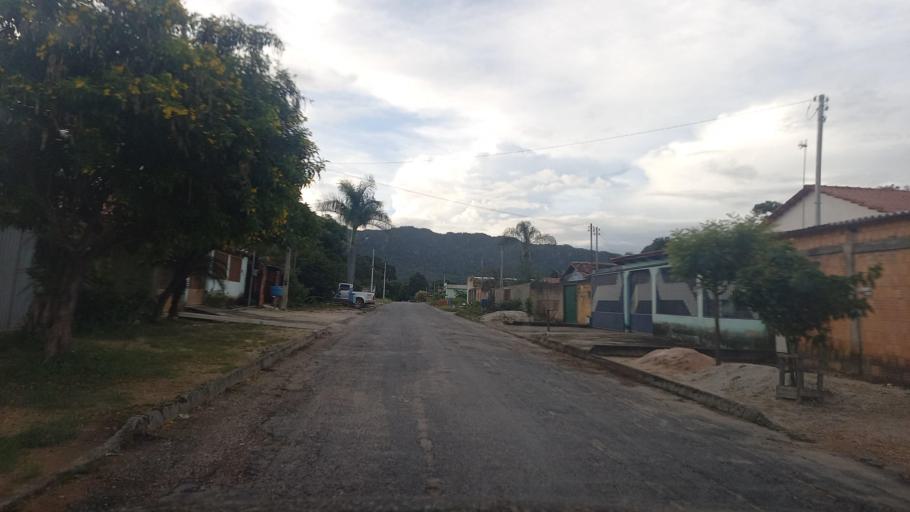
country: BR
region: Goias
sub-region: Cavalcante
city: Cavalcante
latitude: -13.7905
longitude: -47.4583
